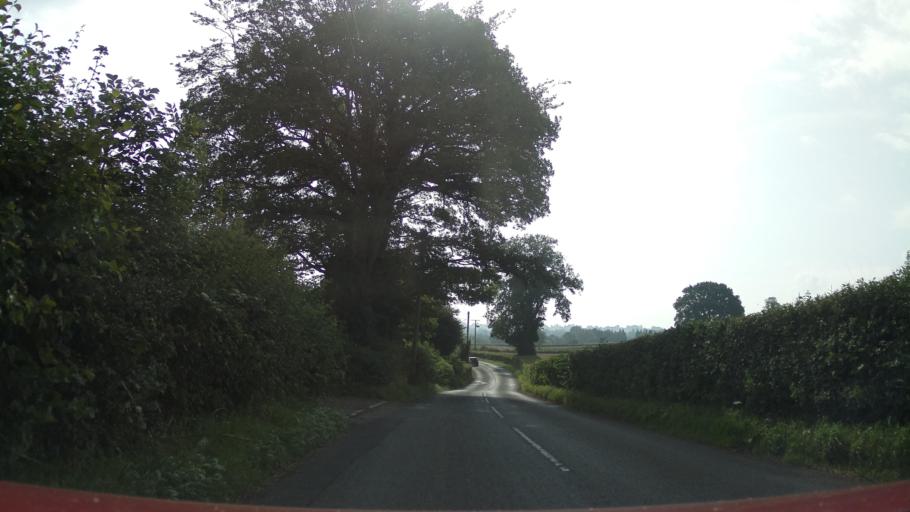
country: GB
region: England
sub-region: Bath and North East Somerset
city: East Harptree
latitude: 51.3012
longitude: -2.6100
